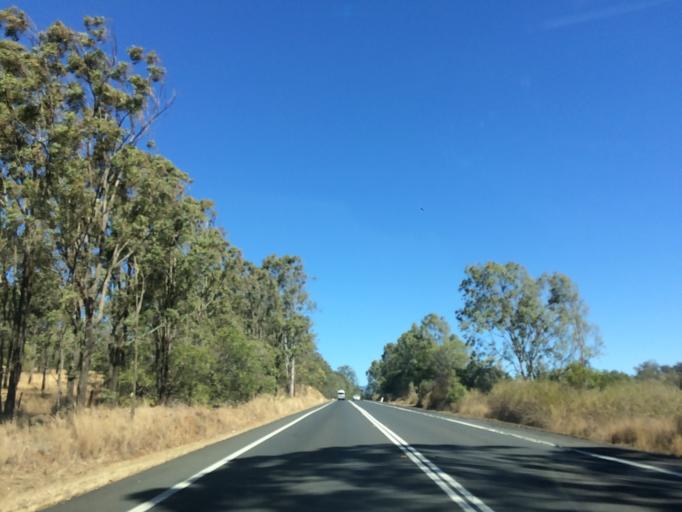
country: AU
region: Queensland
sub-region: Ipswich
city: Thagoona
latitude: -27.9961
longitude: 152.5336
